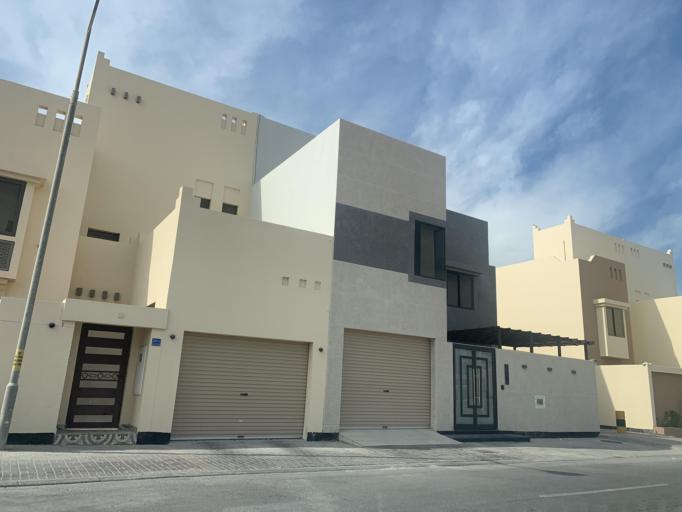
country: BH
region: Central Governorate
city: Madinat Hamad
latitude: 26.1134
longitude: 50.4895
